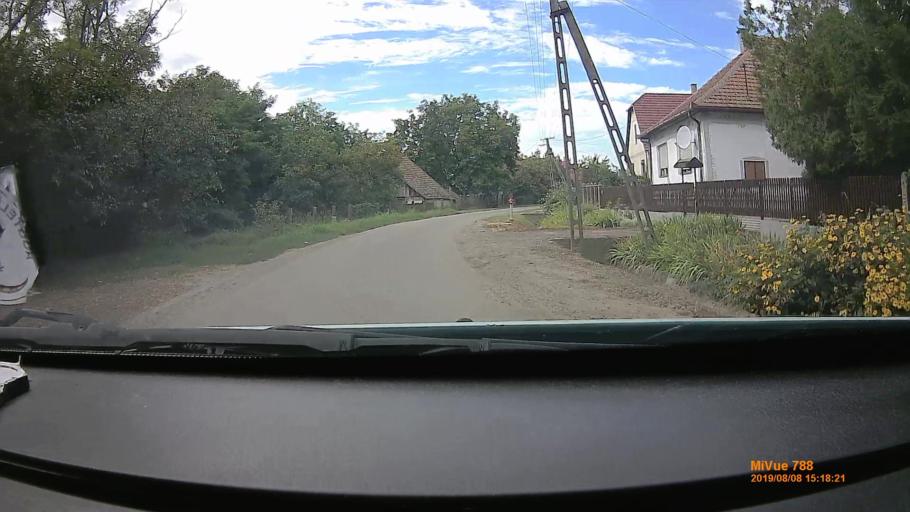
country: HU
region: Szabolcs-Szatmar-Bereg
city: Tunyogmatolcs
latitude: 47.9657
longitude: 22.4582
